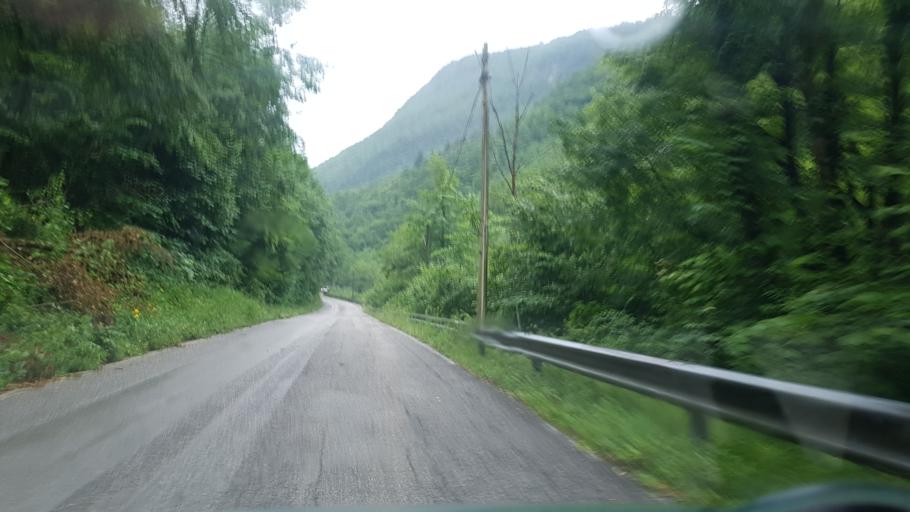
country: IT
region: Friuli Venezia Giulia
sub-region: Provincia di Udine
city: Nimis
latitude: 46.2363
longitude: 13.2867
